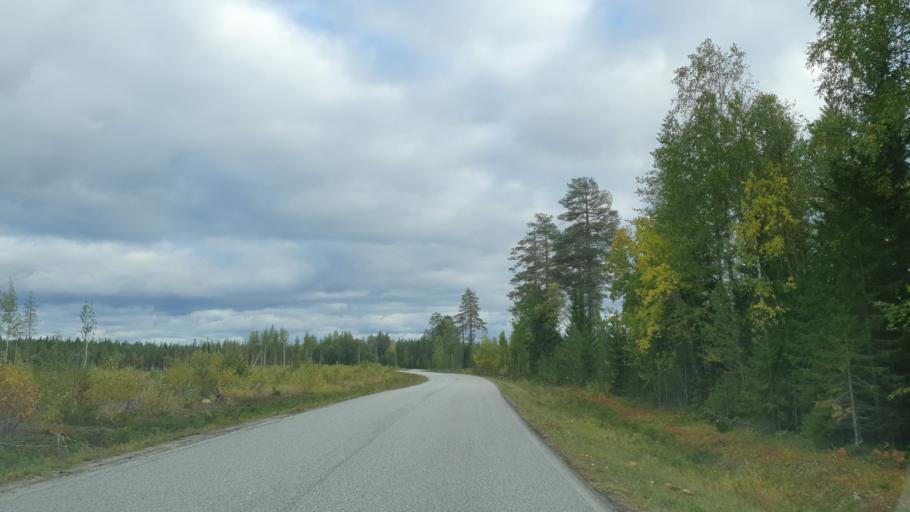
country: FI
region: Kainuu
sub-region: Kehys-Kainuu
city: Kuhmo
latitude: 63.9497
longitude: 29.7551
